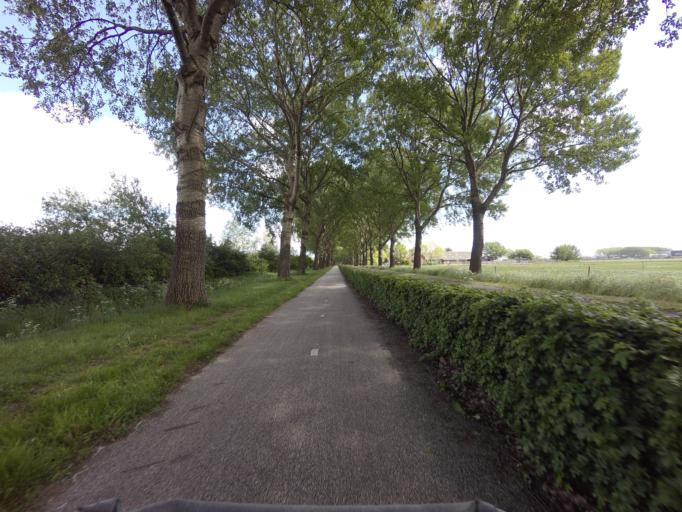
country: NL
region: North Brabant
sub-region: Gemeente Woudrichem
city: Woudrichem
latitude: 51.8482
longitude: 5.0116
